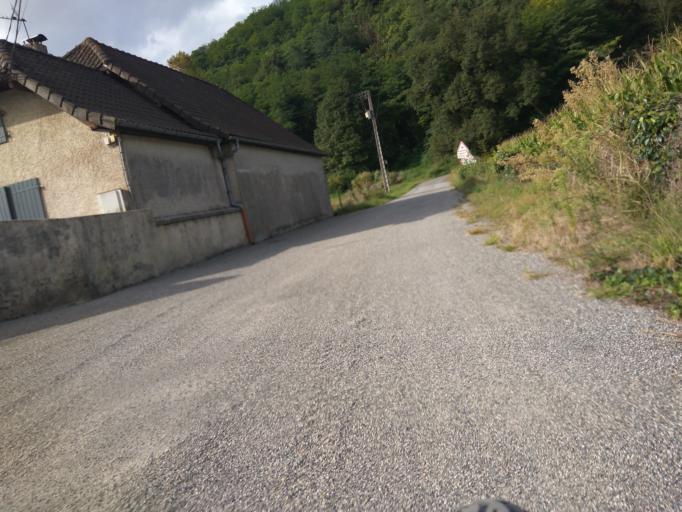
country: FR
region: Aquitaine
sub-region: Departement des Pyrenees-Atlantiques
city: Mazeres-Lezons
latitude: 43.2666
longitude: -0.3439
